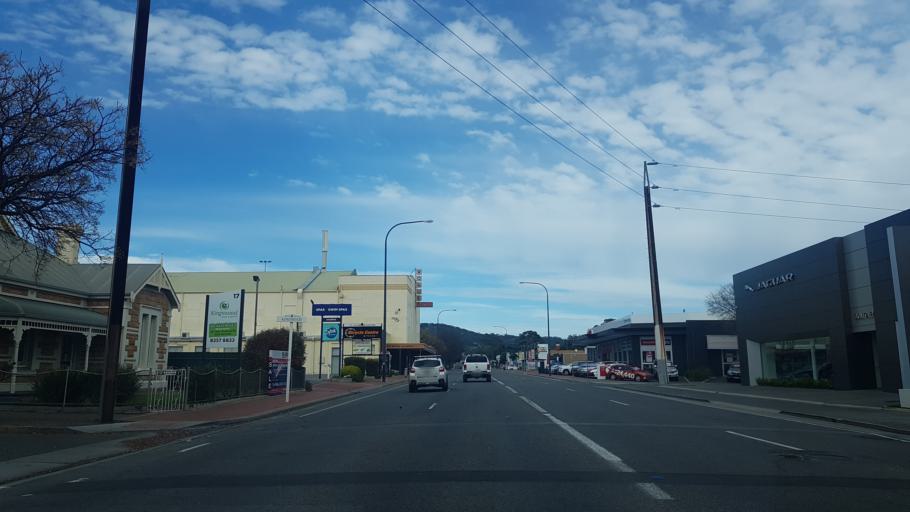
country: AU
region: South Australia
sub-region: Unley
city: Unley Park
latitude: -34.9667
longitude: 138.6087
